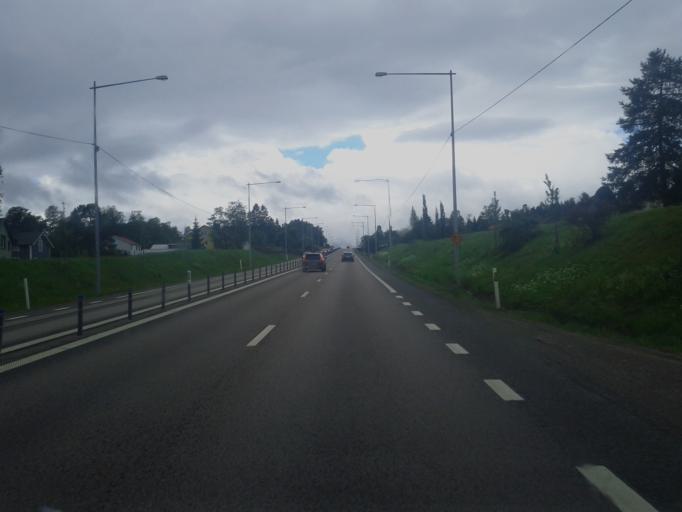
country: SE
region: Vaesternorrland
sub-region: Haernoesands Kommun
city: Haernoesand
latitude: 62.6446
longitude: 17.9069
